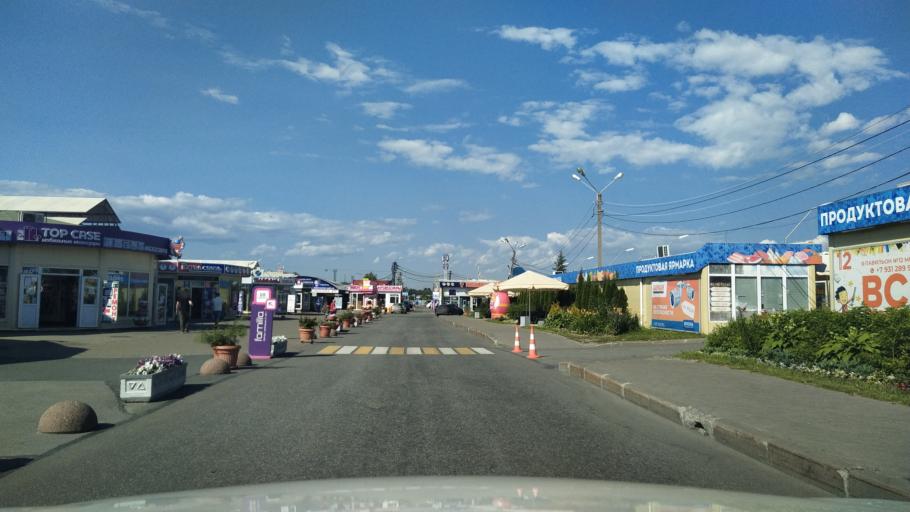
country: RU
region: St.-Petersburg
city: Uritsk
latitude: 59.8616
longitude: 30.2094
